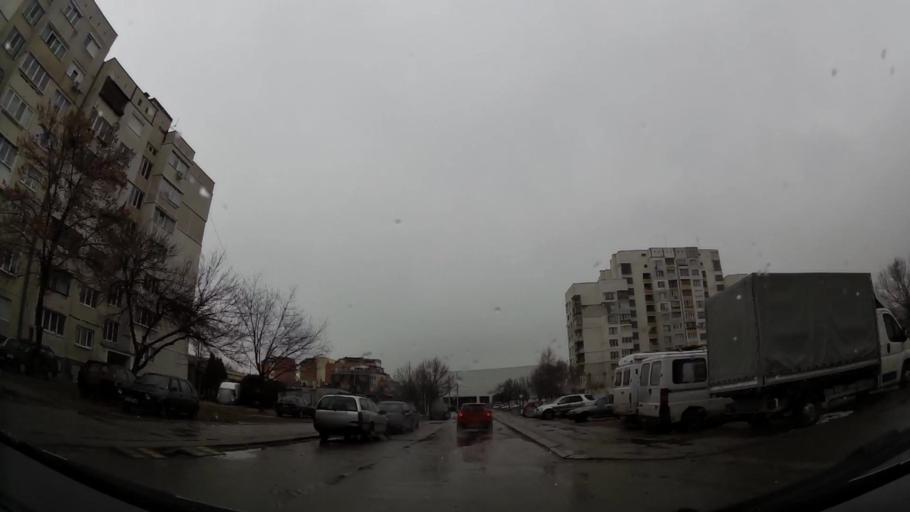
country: BG
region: Sofia-Capital
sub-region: Stolichna Obshtina
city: Sofia
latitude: 42.6416
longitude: 23.4146
